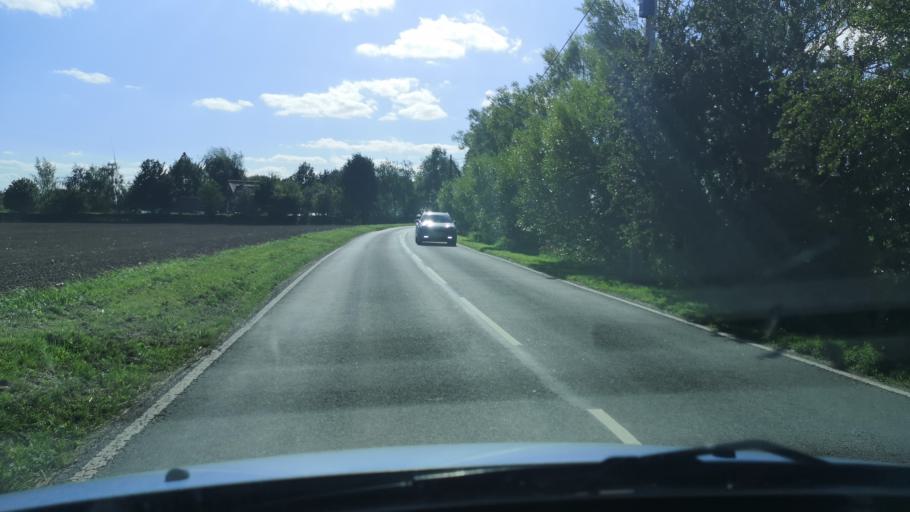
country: GB
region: England
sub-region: North Lincolnshire
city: Eastoft
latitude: 53.6316
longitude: -0.7543
